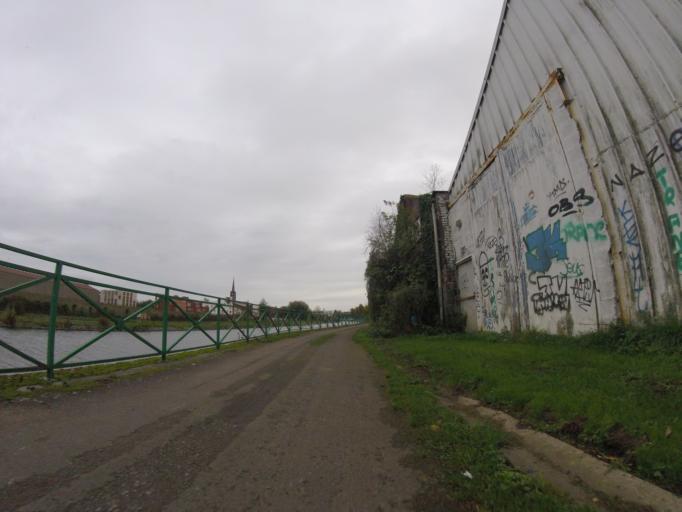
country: FR
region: Nord-Pas-de-Calais
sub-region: Departement du Nord
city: Quesnoy-sur-Deule
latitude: 50.7124
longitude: 2.9936
